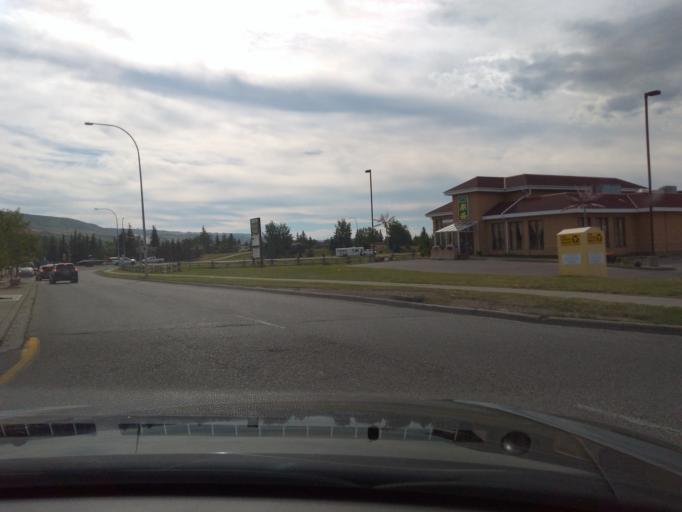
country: CA
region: Alberta
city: Cochrane
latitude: 51.1928
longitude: -114.4890
